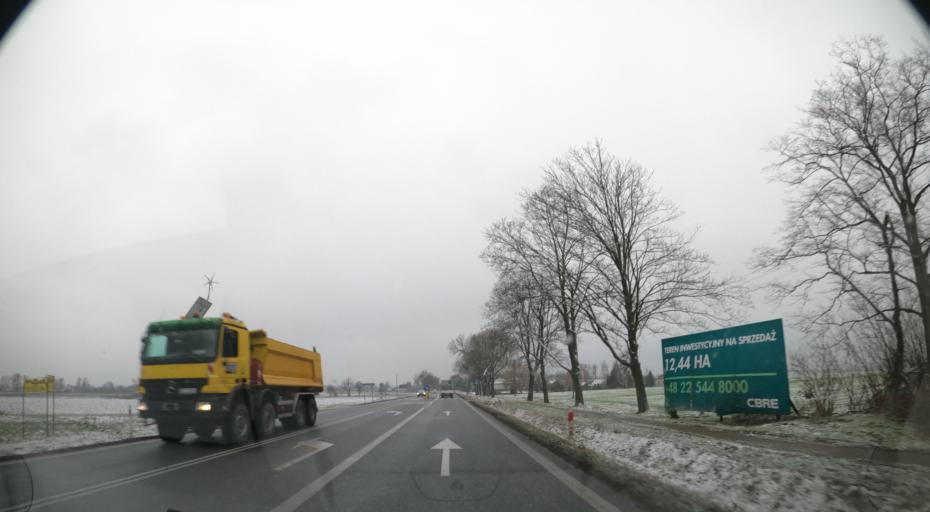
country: PL
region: Masovian Voivodeship
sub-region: Powiat sochaczewski
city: Paprotnia
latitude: 52.2066
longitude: 20.4884
